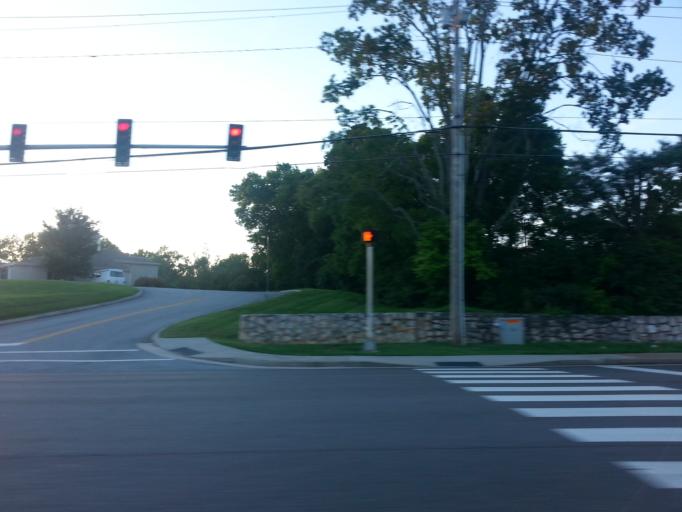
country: US
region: Tennessee
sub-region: Knox County
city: Farragut
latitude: 35.8826
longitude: -84.1574
